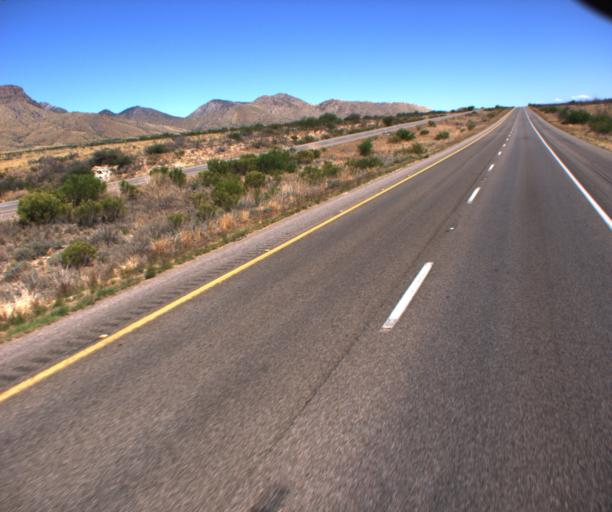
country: US
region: Arizona
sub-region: Cochise County
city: Huachuca City
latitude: 31.7902
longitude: -110.3499
